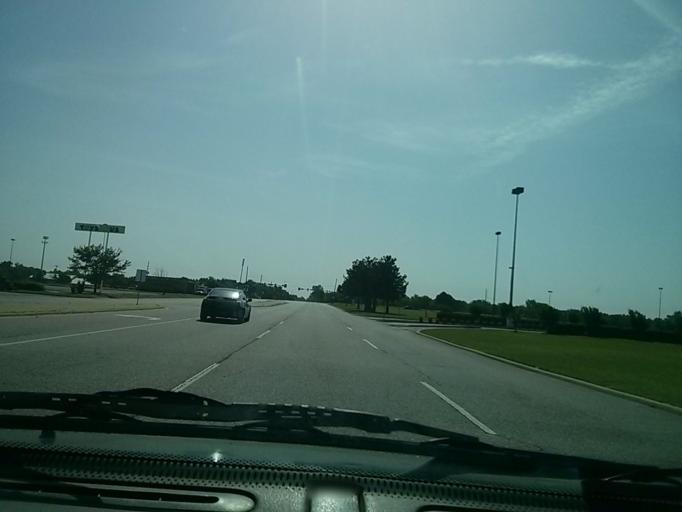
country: US
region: Oklahoma
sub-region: Tulsa County
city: Broken Arrow
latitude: 36.1334
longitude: -95.8185
